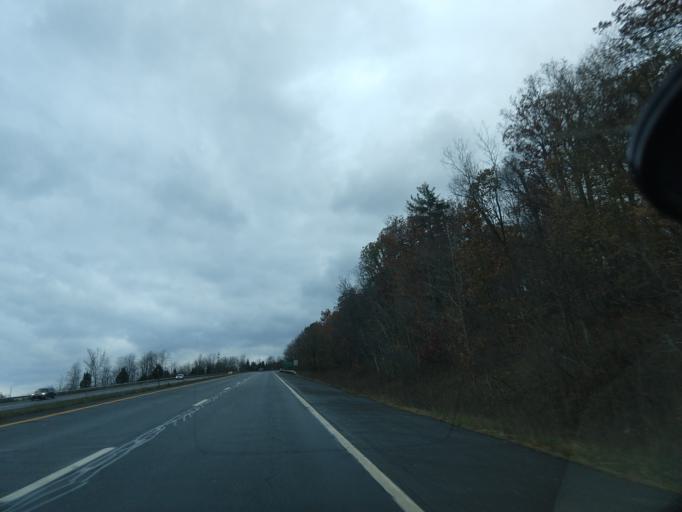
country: US
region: New York
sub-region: Tompkins County
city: Cayuga Heights
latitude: 42.4698
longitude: -76.4998
